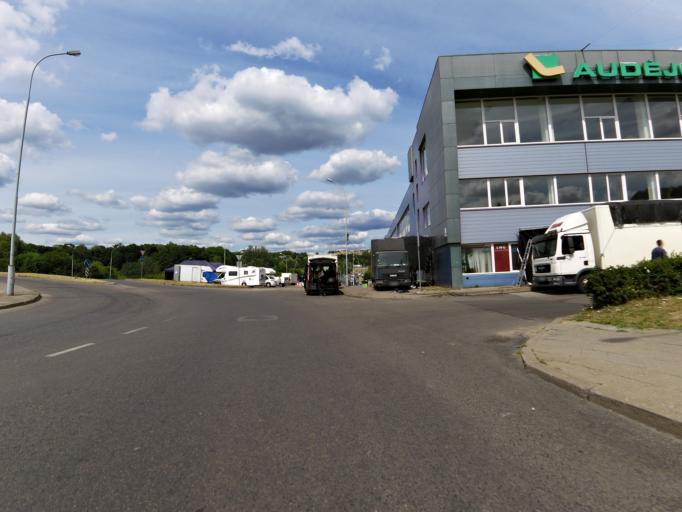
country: LT
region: Vilnius County
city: Rasos
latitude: 54.6769
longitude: 25.3101
